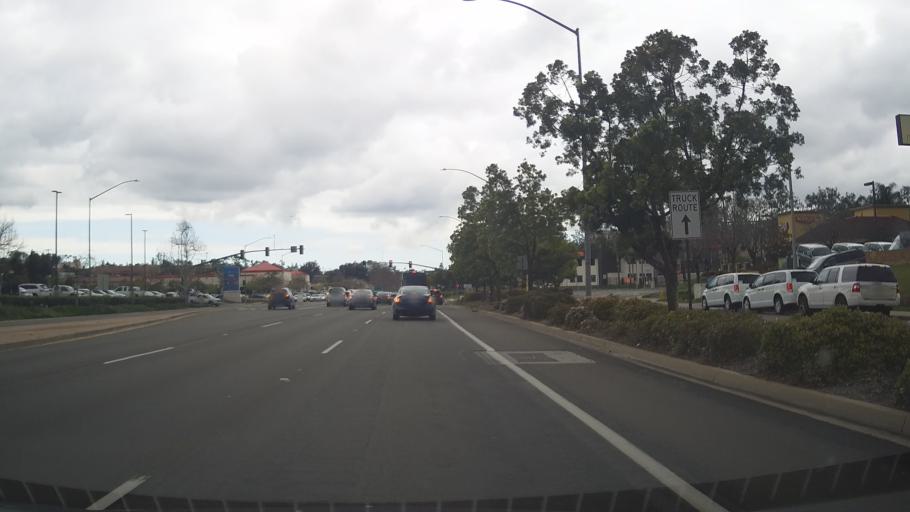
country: US
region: California
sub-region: San Diego County
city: La Mesa
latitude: 32.7759
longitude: -117.0216
